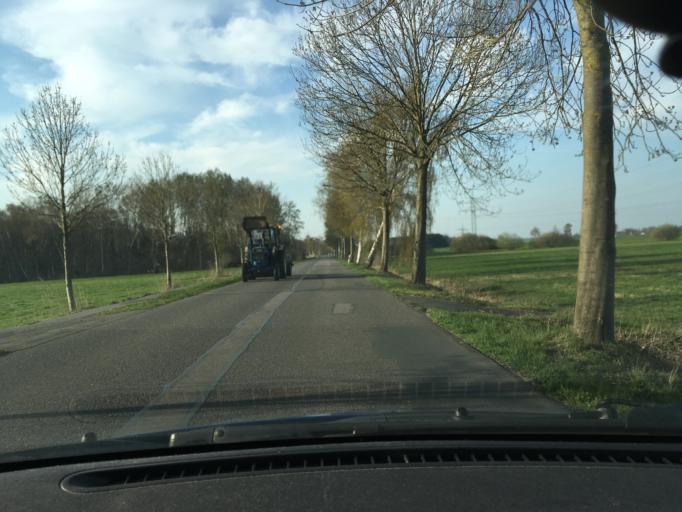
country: DE
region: Lower Saxony
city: Stelle
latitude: 53.4205
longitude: 10.0580
